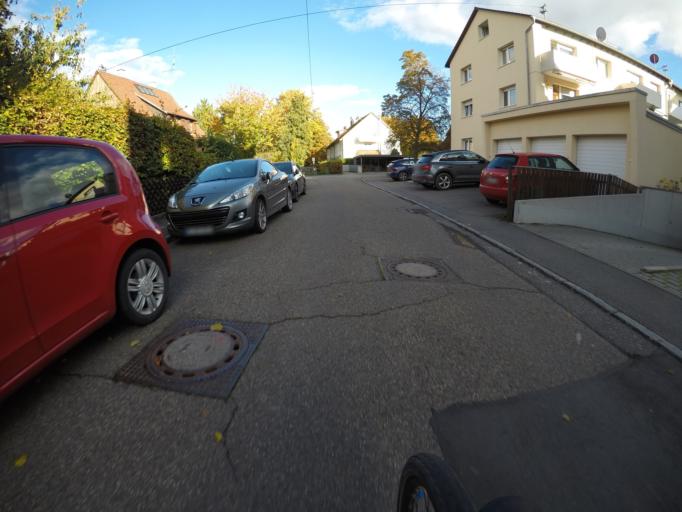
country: DE
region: Baden-Wuerttemberg
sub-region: Regierungsbezirk Stuttgart
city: Filderstadt
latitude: 48.6804
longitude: 9.2239
